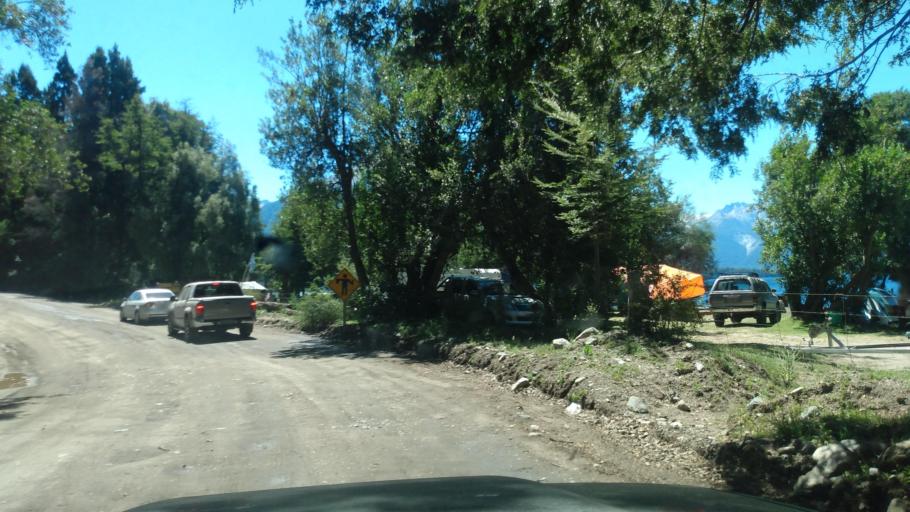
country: AR
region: Neuquen
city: Villa La Angostura
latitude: -40.6271
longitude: -71.4942
